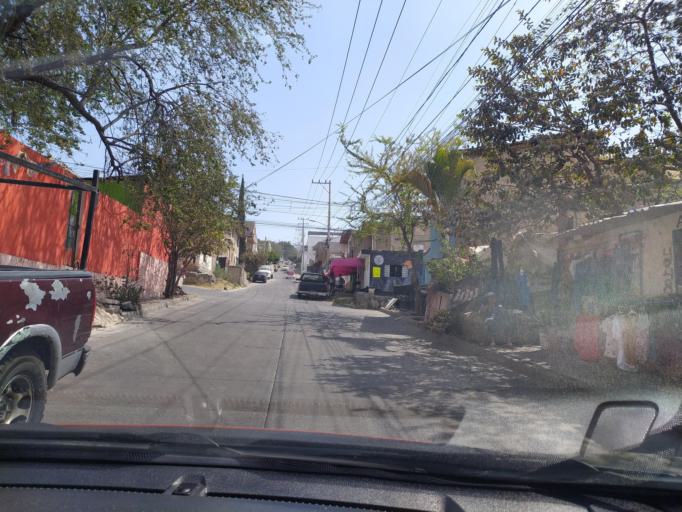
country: MX
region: Jalisco
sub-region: Tlajomulco de Zuniga
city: Altus Bosques
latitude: 20.6110
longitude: -103.3687
